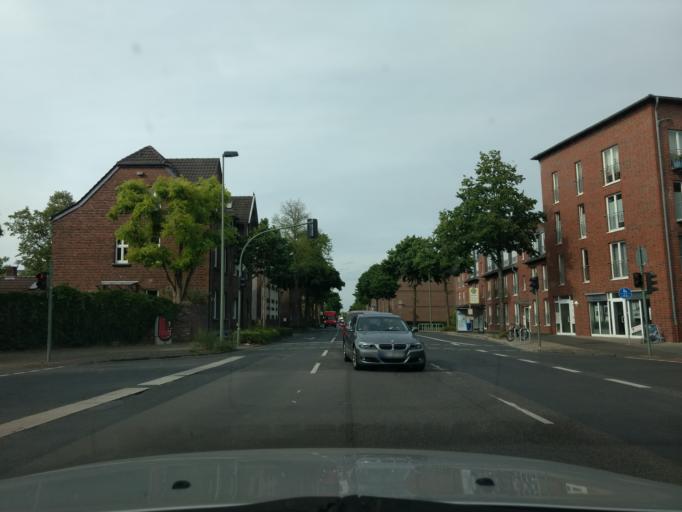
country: DE
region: North Rhine-Westphalia
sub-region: Regierungsbezirk Dusseldorf
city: Meerbusch
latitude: 51.3044
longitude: 6.6724
